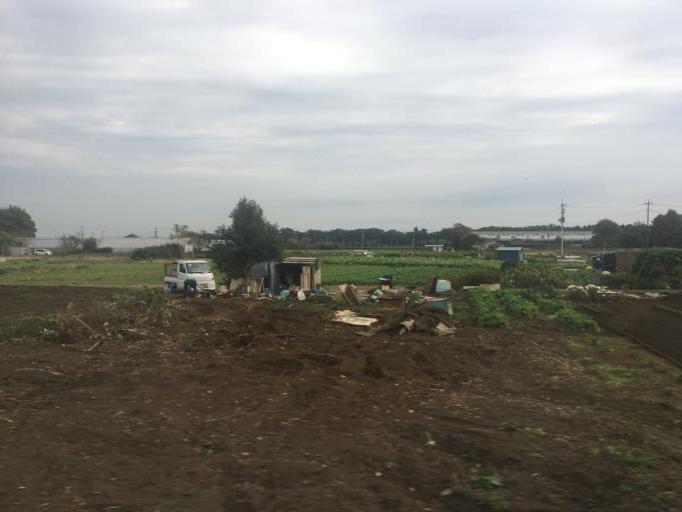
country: JP
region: Saitama
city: Hanno
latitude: 35.8014
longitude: 139.3334
